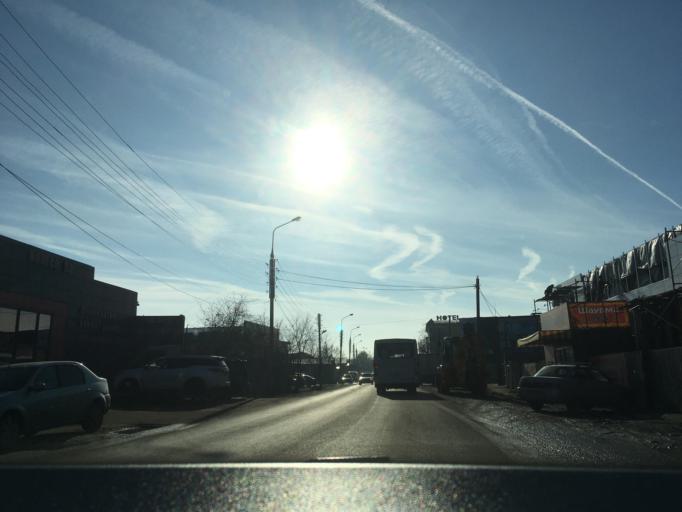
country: RU
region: Krasnodarskiy
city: Krasnodar
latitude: 45.1257
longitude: 39.0110
